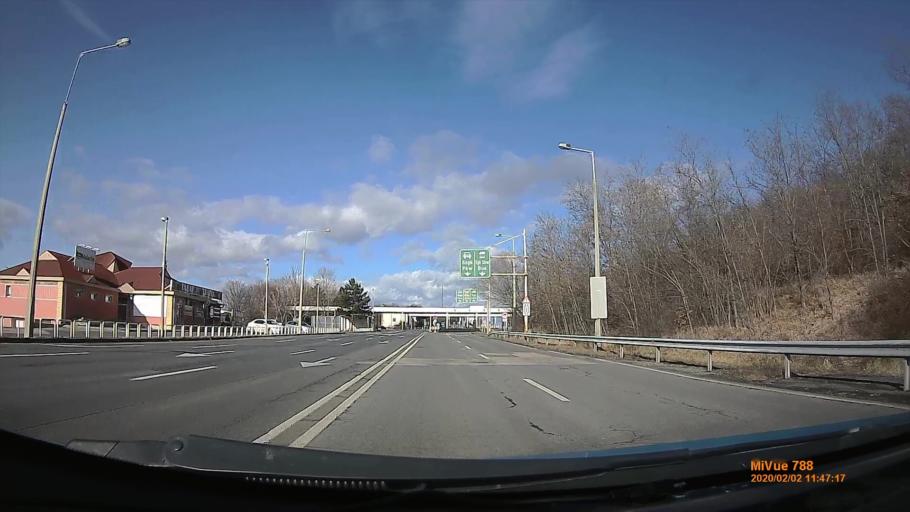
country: AT
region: Burgenland
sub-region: Eisenstadt-Umgebung
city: Klingenbach
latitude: 47.7387
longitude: 16.5475
